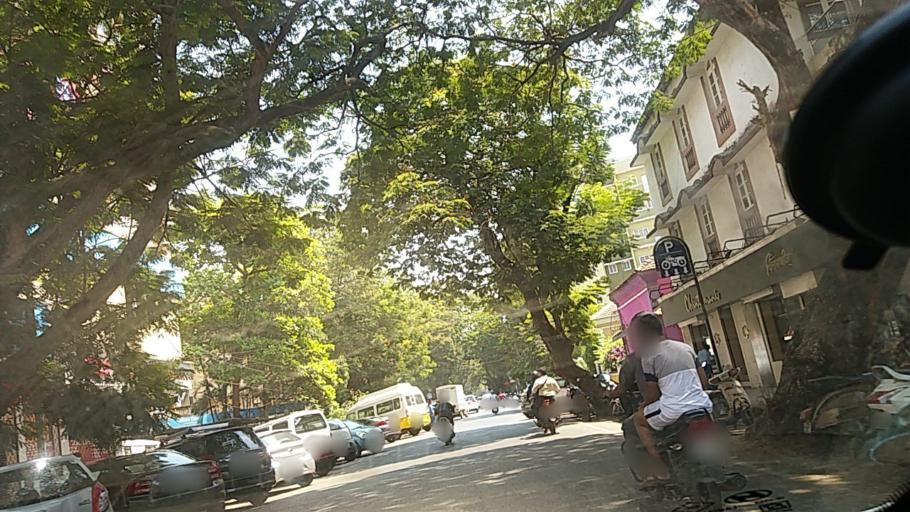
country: IN
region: Goa
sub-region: North Goa
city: Panaji
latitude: 15.4965
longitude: 73.8236
